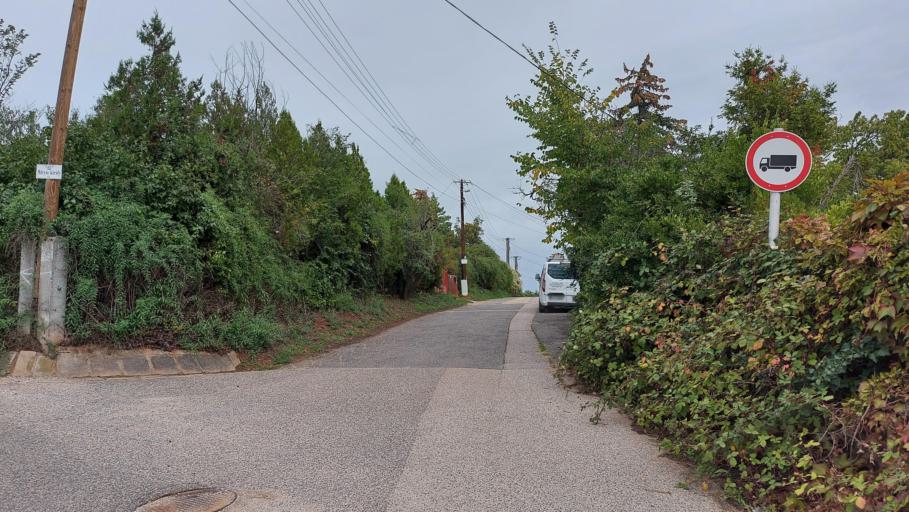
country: HU
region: Veszprem
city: Balatonalmadi
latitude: 47.0267
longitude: 18.0067
